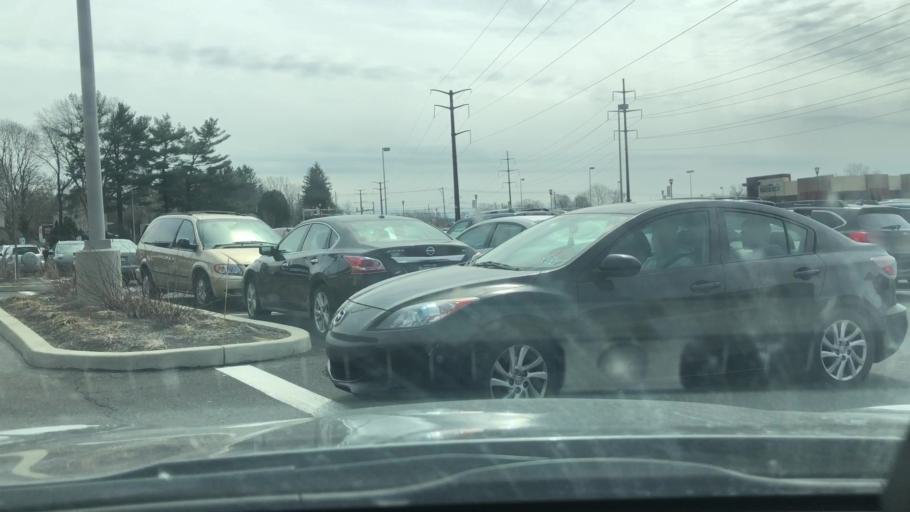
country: US
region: Pennsylvania
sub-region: Lehigh County
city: Wescosville
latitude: 40.5648
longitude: -75.5624
